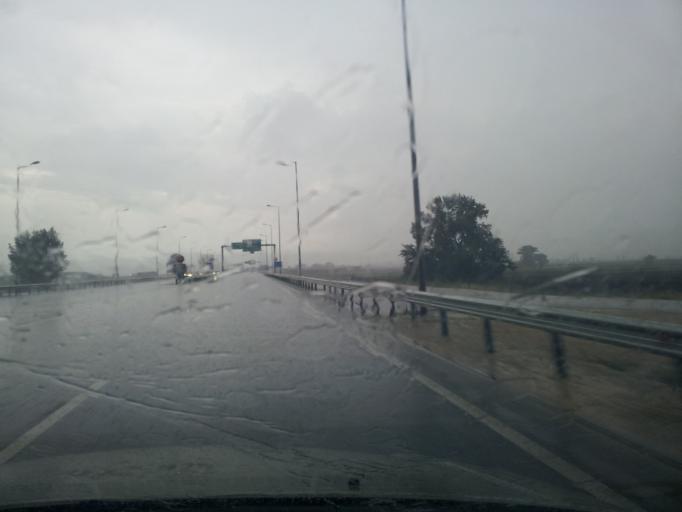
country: HU
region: Borsod-Abauj-Zemplen
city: Arnot
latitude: 48.1150
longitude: 20.8513
